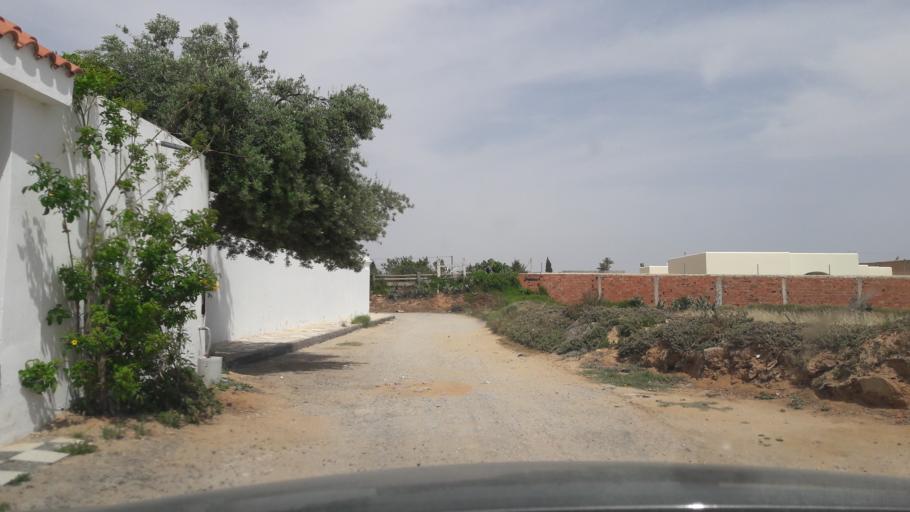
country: TN
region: Safaqis
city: Sfax
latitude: 34.7856
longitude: 10.7553
